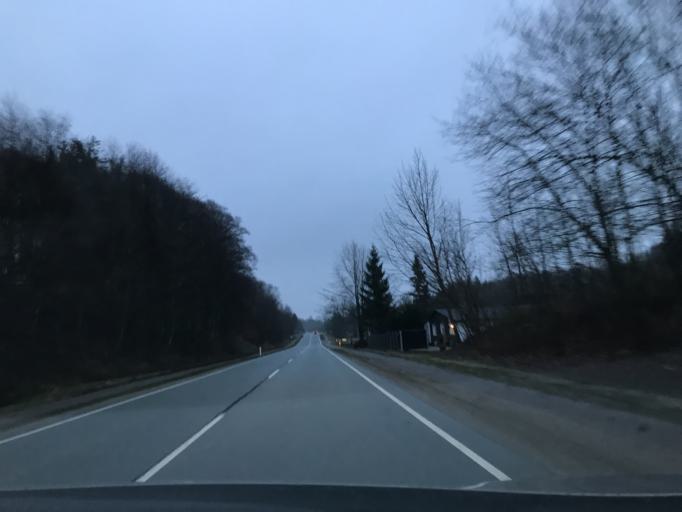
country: DK
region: Central Jutland
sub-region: Hedensted Kommune
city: Hedensted
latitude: 55.7126
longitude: 9.7400
